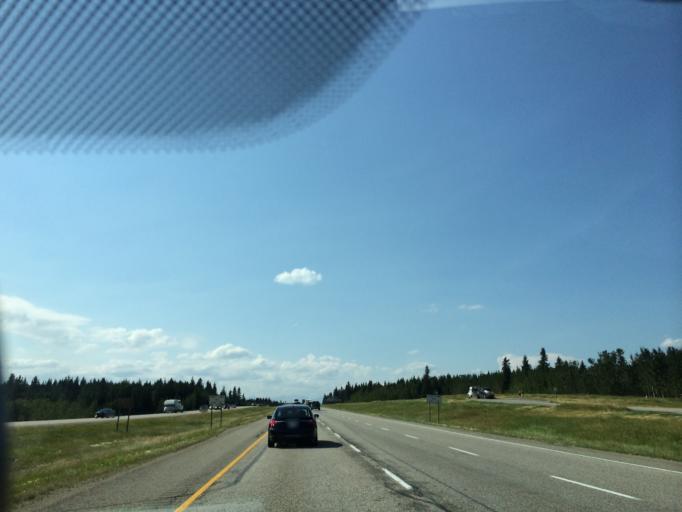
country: CA
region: Alberta
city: Cochrane
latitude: 51.1432
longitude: -114.7240
